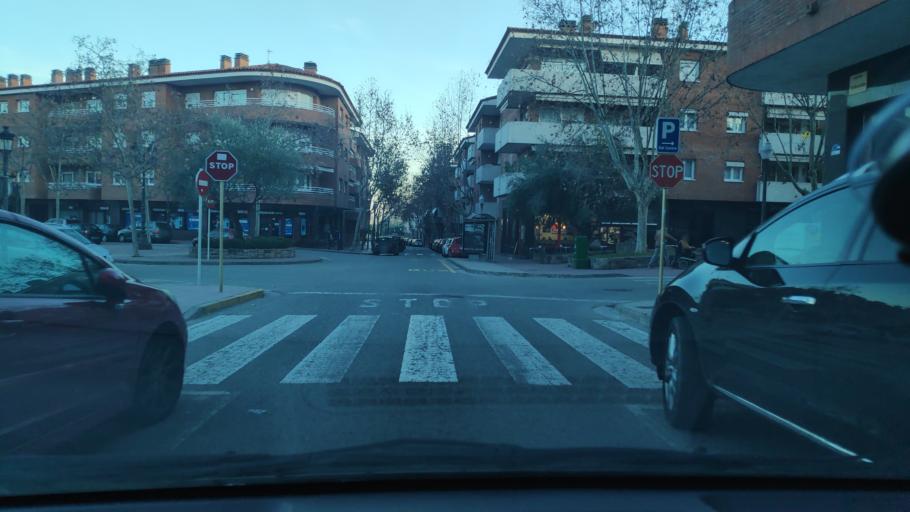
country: ES
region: Catalonia
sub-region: Provincia de Barcelona
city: Sant Quirze del Valles
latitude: 41.5325
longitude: 2.0842
